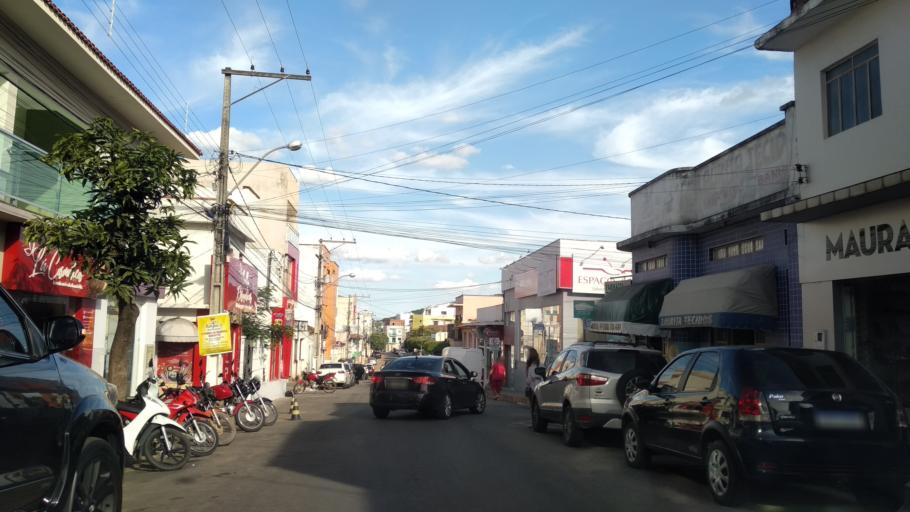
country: BR
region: Bahia
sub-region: Caetite
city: Caetite
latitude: -14.0676
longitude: -42.4903
